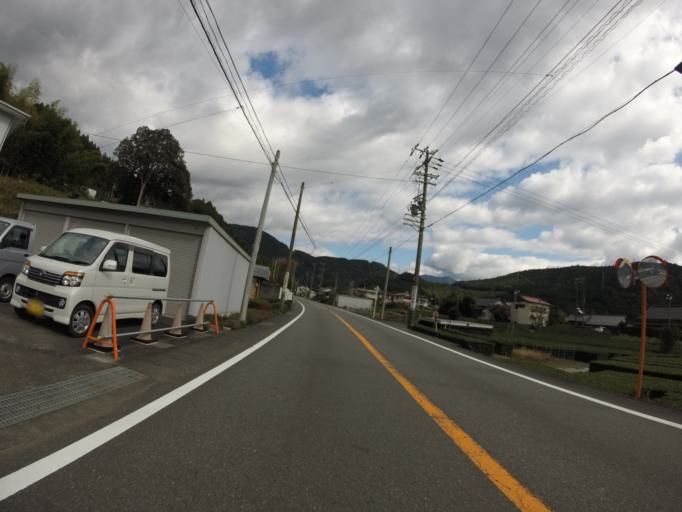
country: JP
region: Shizuoka
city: Kanaya
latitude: 35.0837
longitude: 138.1043
